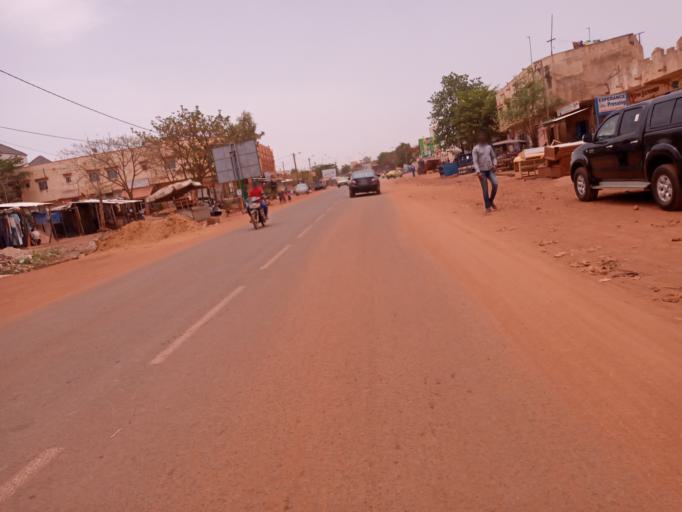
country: ML
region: Bamako
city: Bamako
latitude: 12.5748
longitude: -8.0086
